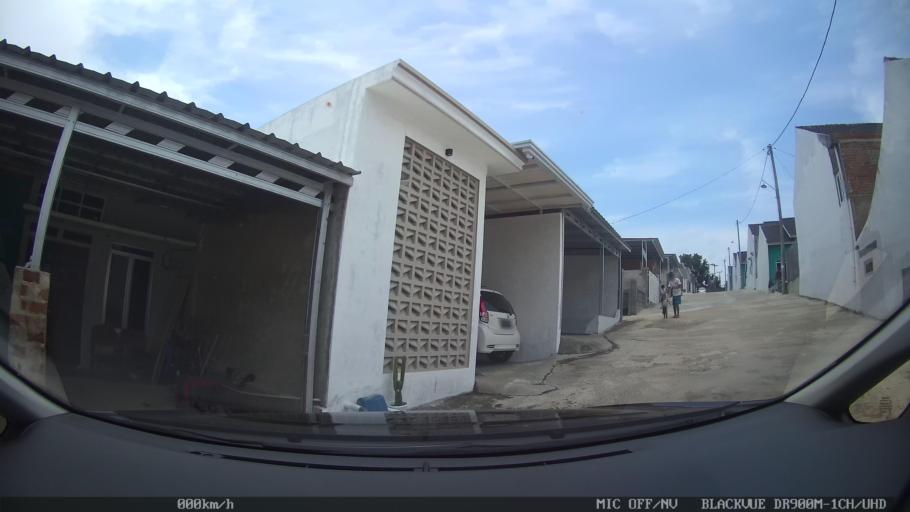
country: ID
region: Lampung
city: Bandarlampung
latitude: -5.4056
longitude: 105.2023
